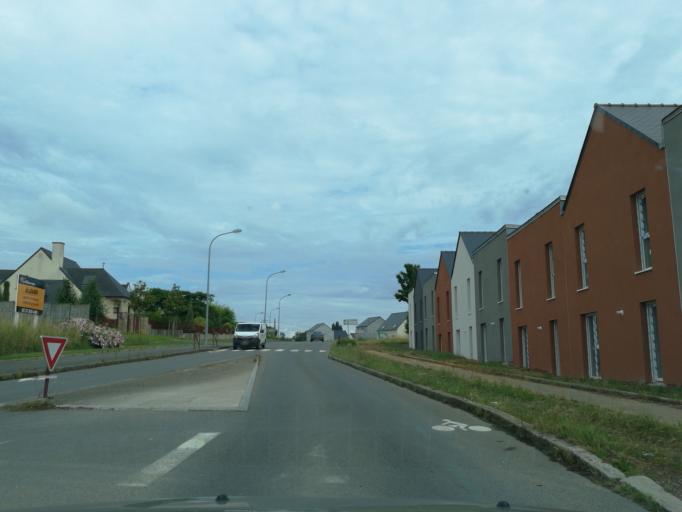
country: FR
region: Brittany
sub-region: Departement d'Ille-et-Vilaine
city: Montauban-de-Bretagne
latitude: 48.1958
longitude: -2.0375
